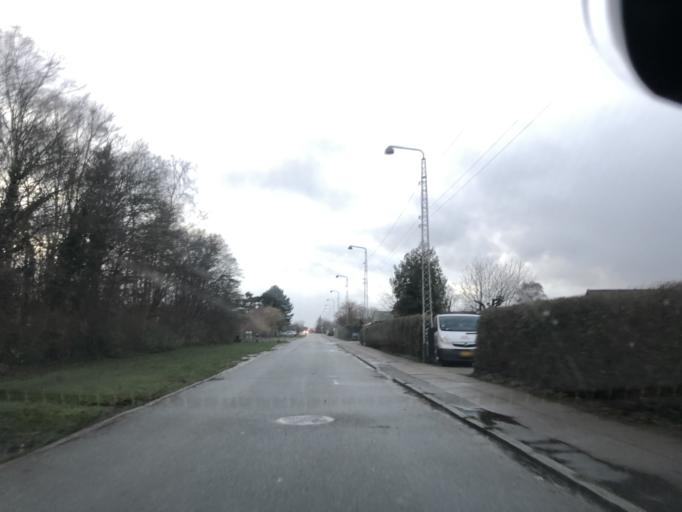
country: DK
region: Capital Region
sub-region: Tarnby Kommune
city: Tarnby
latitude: 55.6104
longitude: 12.5970
